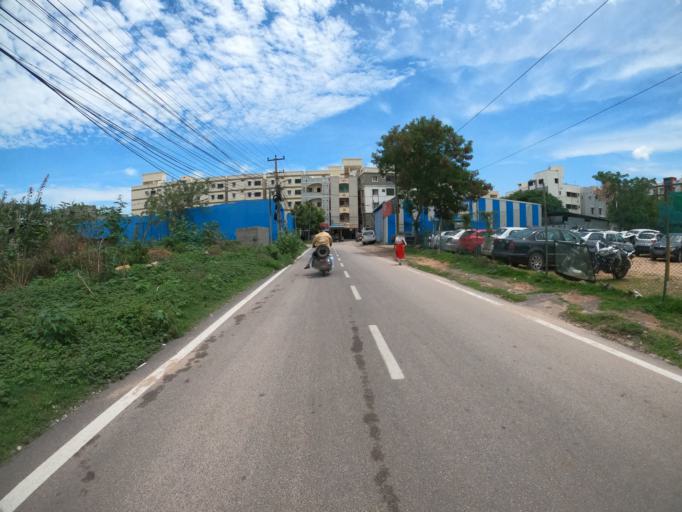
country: IN
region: Telangana
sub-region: Hyderabad
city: Hyderabad
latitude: 17.3684
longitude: 78.4223
